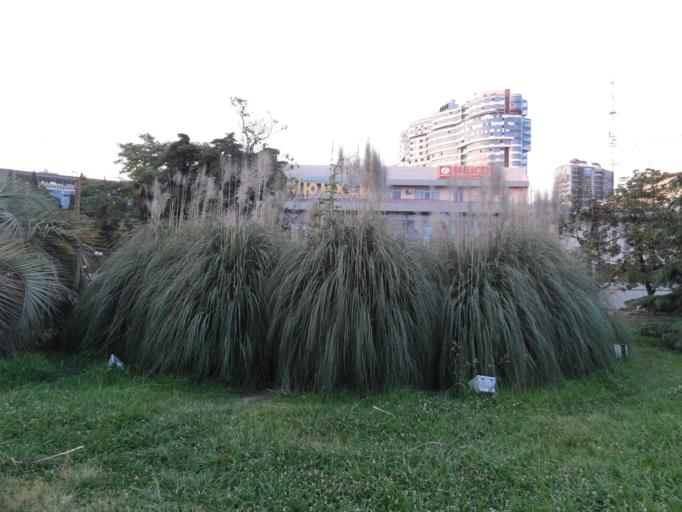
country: RU
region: Krasnodarskiy
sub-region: Sochi City
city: Sochi
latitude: 43.5818
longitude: 39.7203
